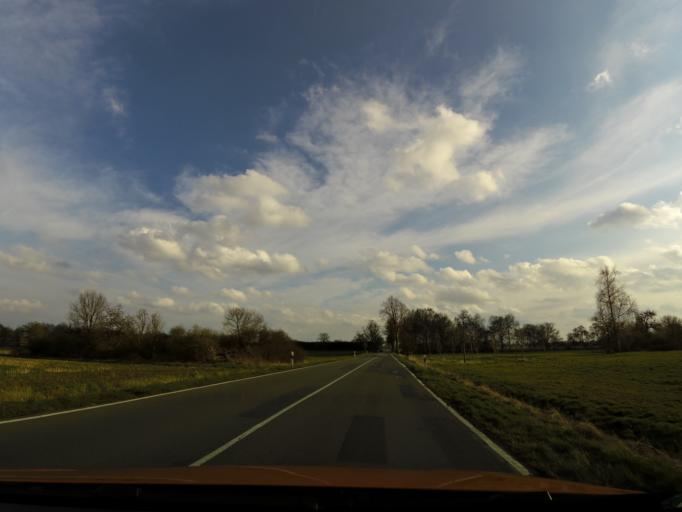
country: DE
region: Lower Saxony
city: Rethem
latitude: 52.7773
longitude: 9.3763
